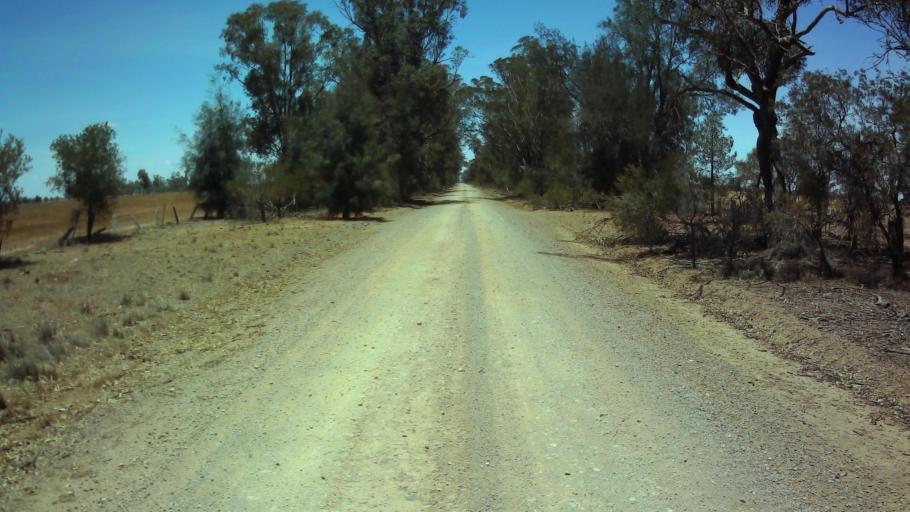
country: AU
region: New South Wales
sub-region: Weddin
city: Grenfell
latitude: -33.9375
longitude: 147.7125
